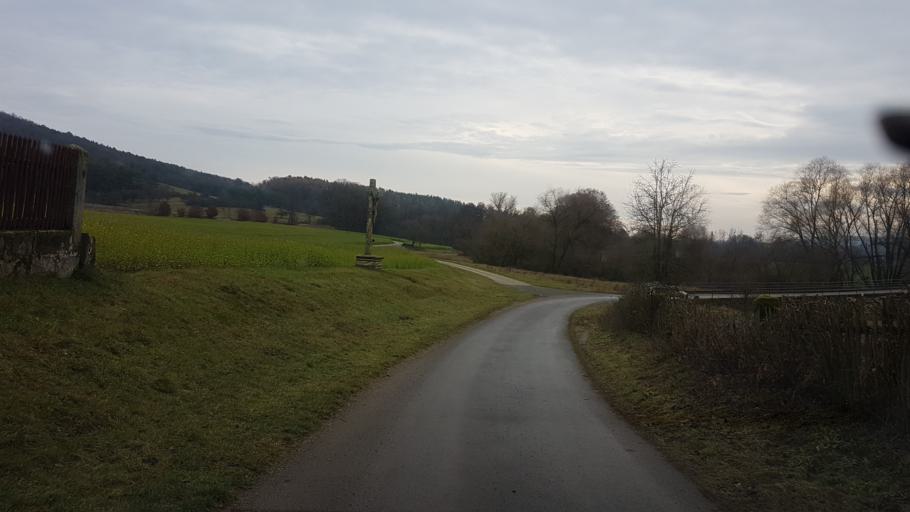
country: DE
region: Bavaria
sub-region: Upper Franconia
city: Reckendorf
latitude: 50.0061
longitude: 10.8389
